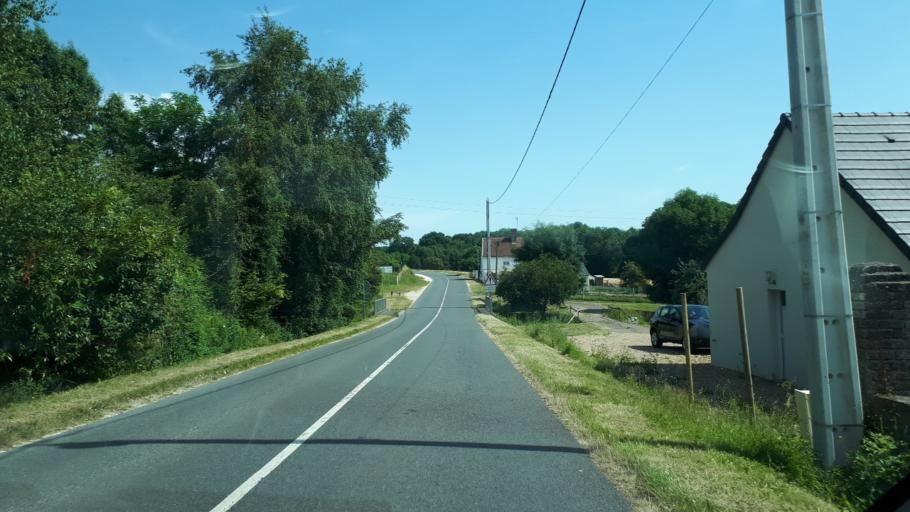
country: FR
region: Centre
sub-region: Departement du Loir-et-Cher
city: La Ville-aux-Clercs
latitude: 47.9237
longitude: 1.0839
